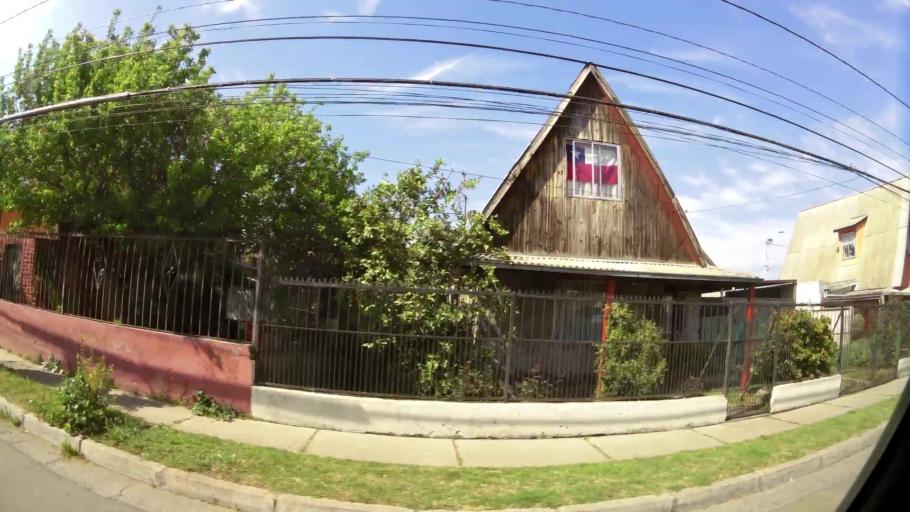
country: CL
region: Santiago Metropolitan
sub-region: Provincia de Talagante
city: Talagante
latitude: -33.6754
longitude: -70.9467
